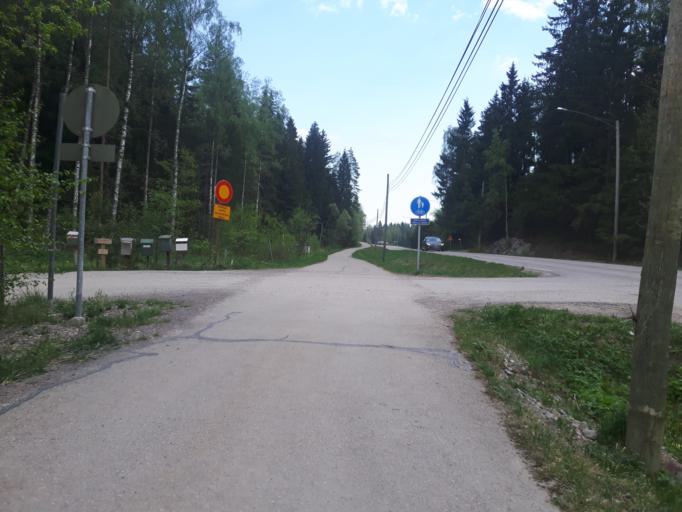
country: FI
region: Uusimaa
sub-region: Porvoo
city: Porvoo
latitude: 60.3971
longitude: 25.7320
